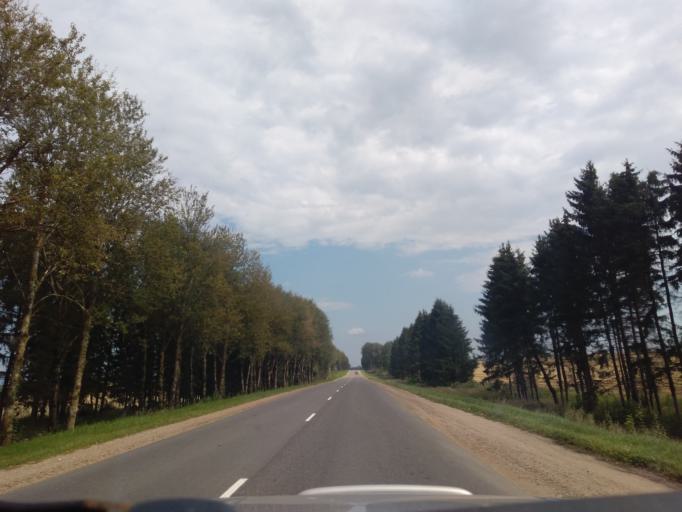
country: BY
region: Minsk
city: Khatsyezhyna
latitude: 53.9125
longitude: 27.3299
